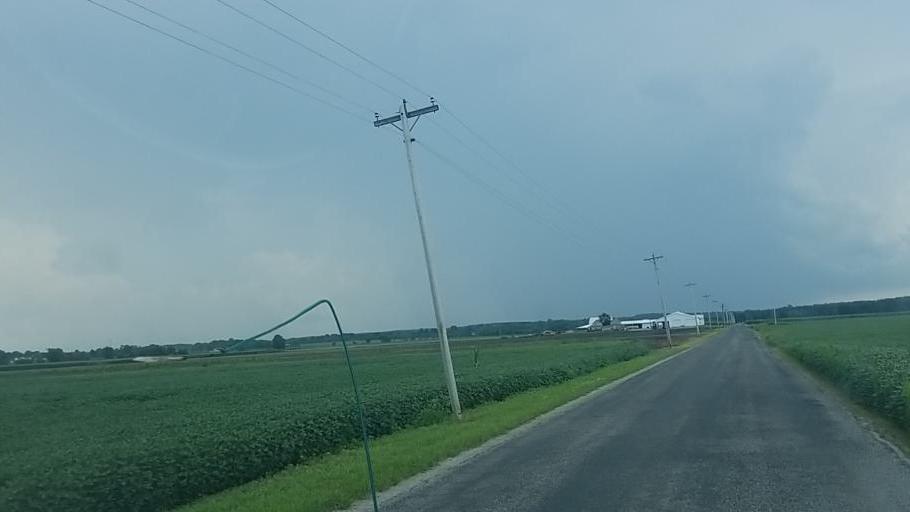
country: US
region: Ohio
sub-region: Medina County
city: Lodi
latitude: 41.0120
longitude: -82.0185
